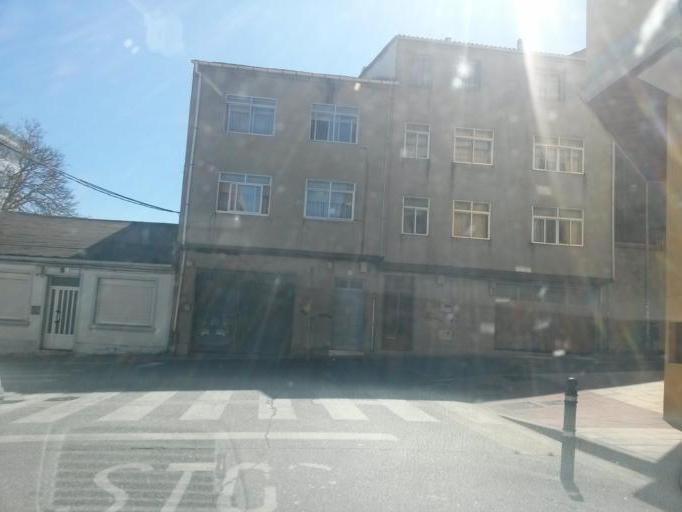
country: ES
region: Galicia
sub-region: Provincia de Lugo
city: Lugo
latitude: 43.0261
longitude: -7.5707
